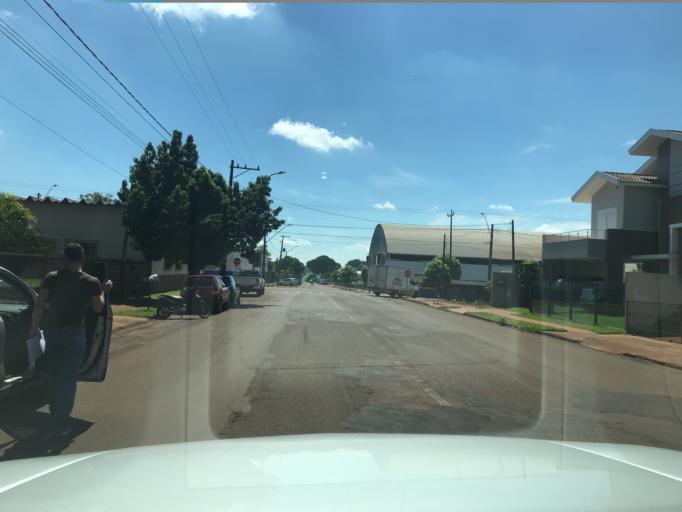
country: BR
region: Parana
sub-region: Palotina
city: Palotina
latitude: -24.2846
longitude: -53.8364
